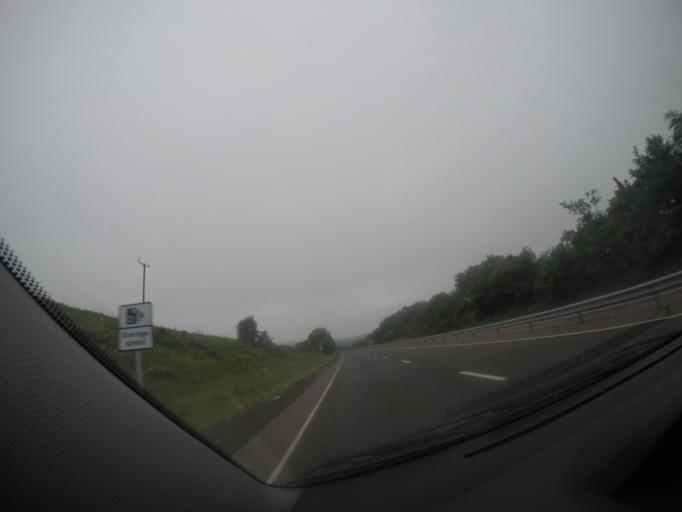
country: GB
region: Scotland
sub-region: Angus
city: Forfar
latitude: 56.5815
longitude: -2.9131
